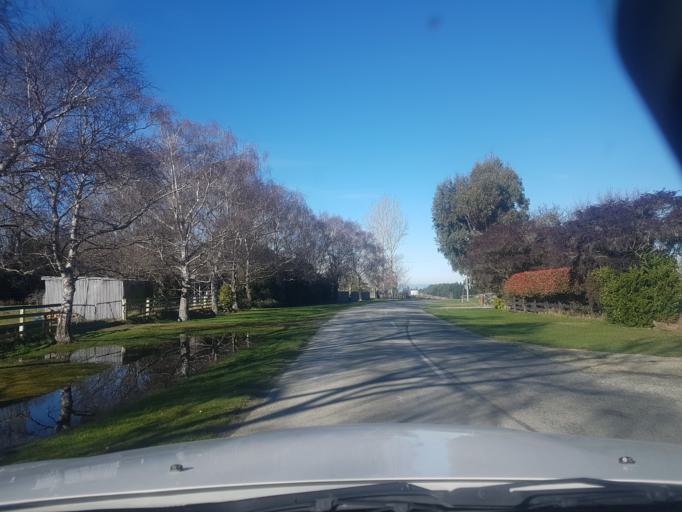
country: NZ
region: Canterbury
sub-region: Timaru District
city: Pleasant Point
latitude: -44.3726
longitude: 171.0777
